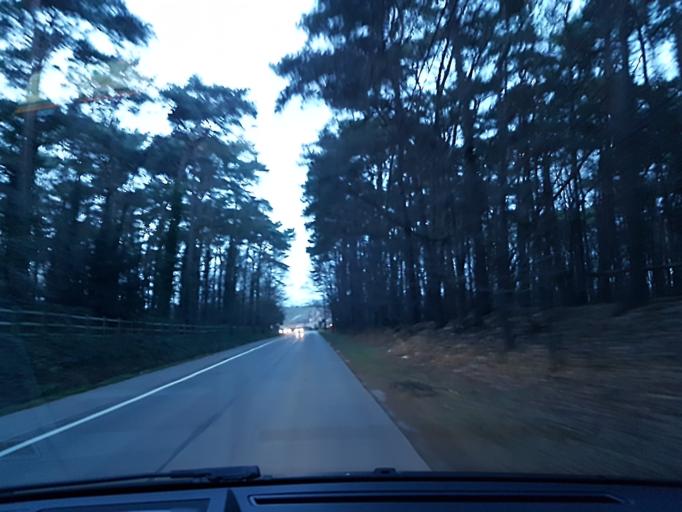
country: BE
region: Flanders
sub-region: Provincie Vlaams-Brabant
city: Boortmeerbeek
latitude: 50.9876
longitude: 4.5995
